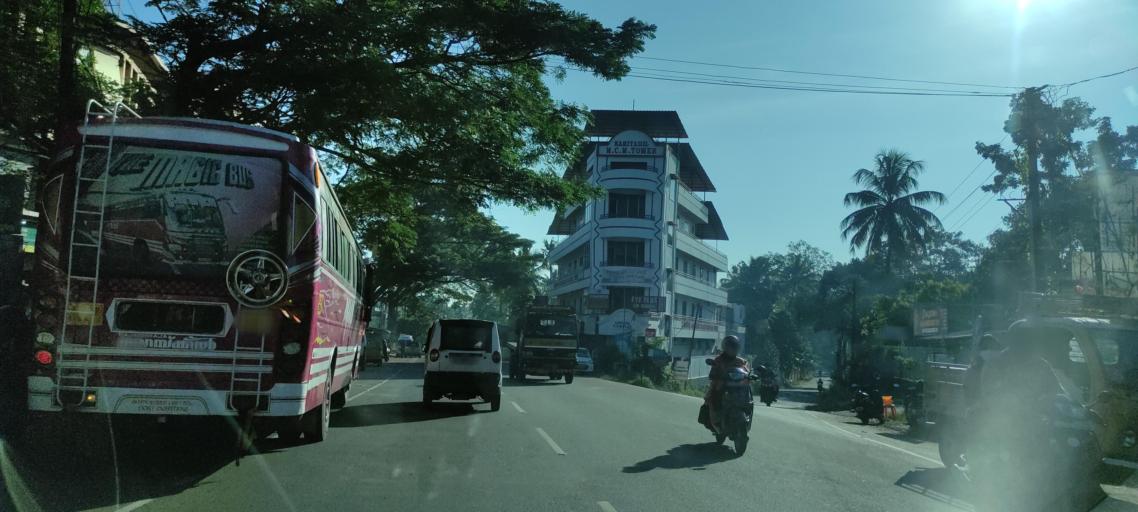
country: IN
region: Kerala
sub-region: Alappuzha
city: Kattanam
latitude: 9.1764
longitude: 76.5647
